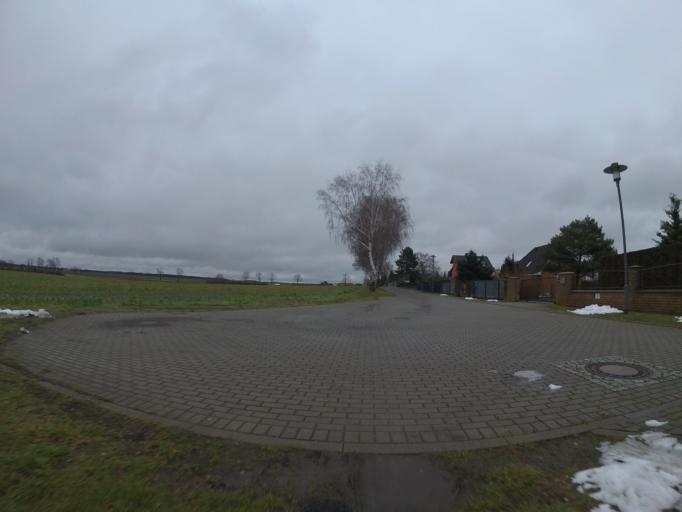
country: DE
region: Brandenburg
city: Ahrensfelde
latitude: 52.5710
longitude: 13.5901
